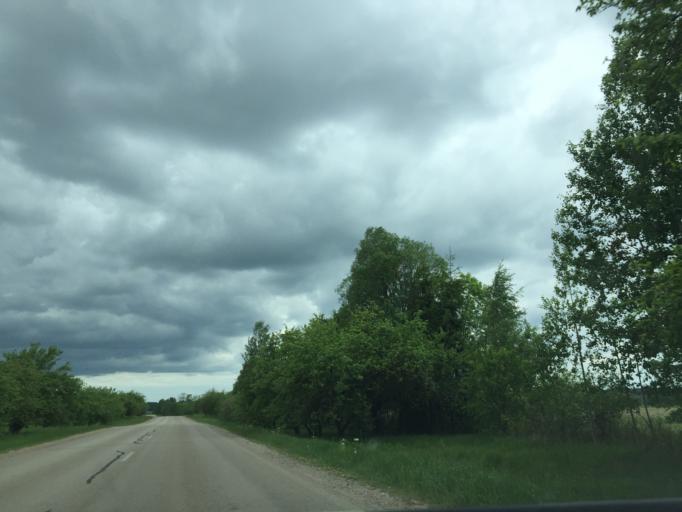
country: LV
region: Dagda
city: Dagda
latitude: 56.1000
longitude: 27.5148
